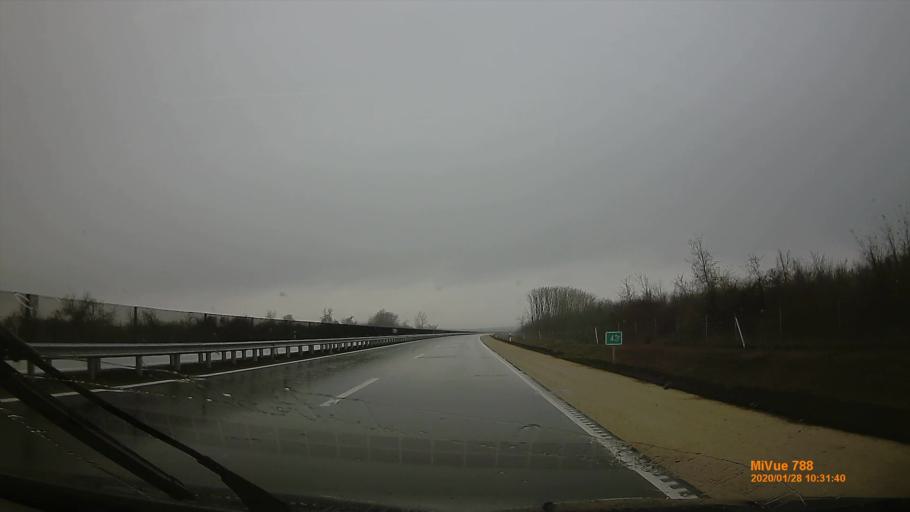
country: HU
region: Pest
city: Gomba
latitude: 47.3417
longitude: 19.5006
